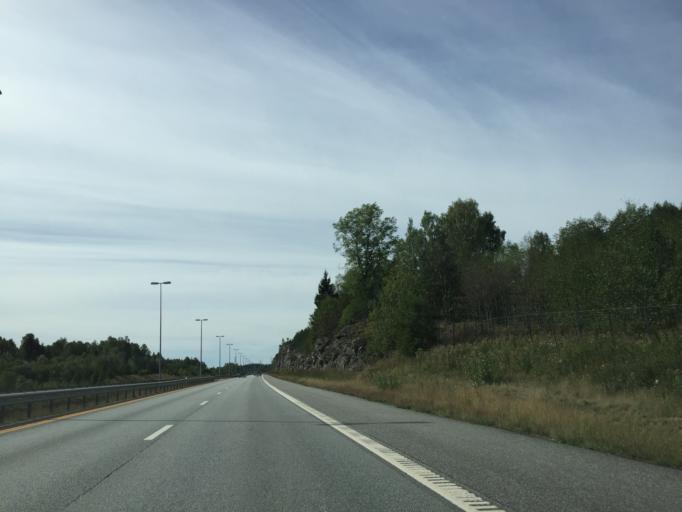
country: NO
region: Akershus
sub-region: Vestby
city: Vestby
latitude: 59.5807
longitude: 10.7311
